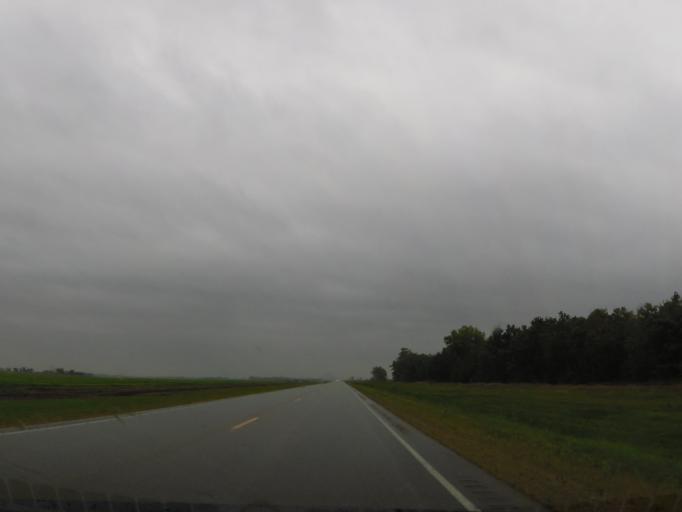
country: US
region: Minnesota
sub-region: Marshall County
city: Warren
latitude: 48.2813
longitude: -96.8017
